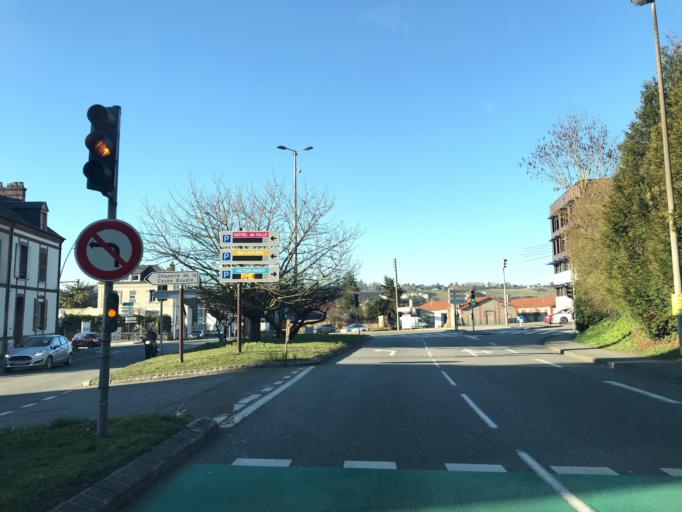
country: FR
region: Haute-Normandie
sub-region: Departement de l'Eure
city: Evreux
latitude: 49.0180
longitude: 1.1430
